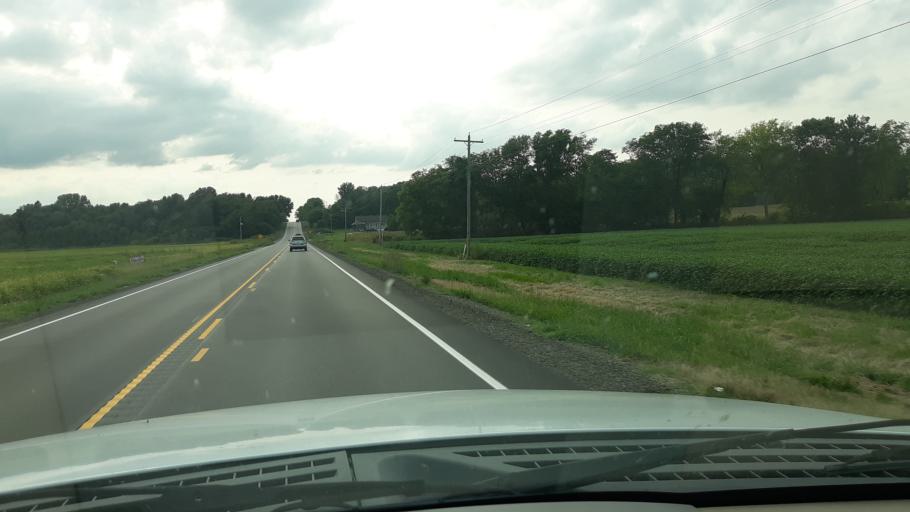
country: US
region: Indiana
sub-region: Gibson County
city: Princeton
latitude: 38.3558
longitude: -87.6486
